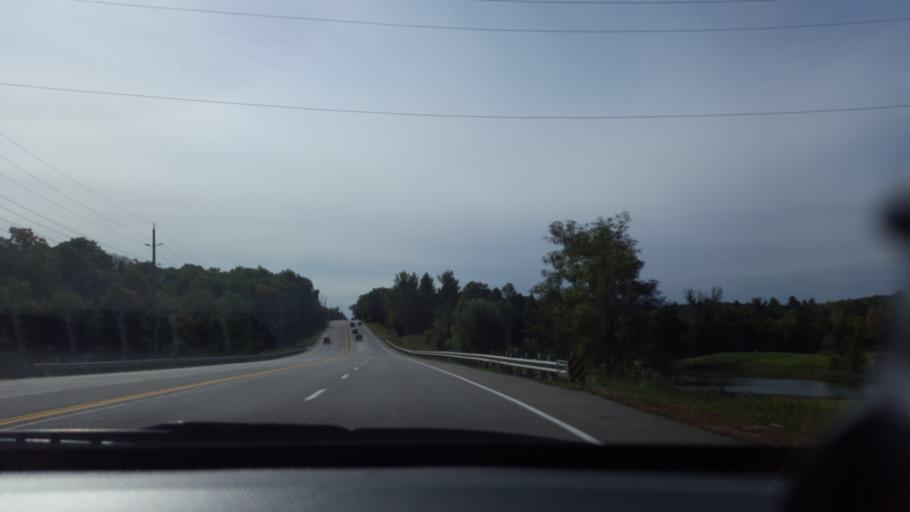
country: CA
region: Ontario
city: Newmarket
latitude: 43.9815
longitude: -79.4916
